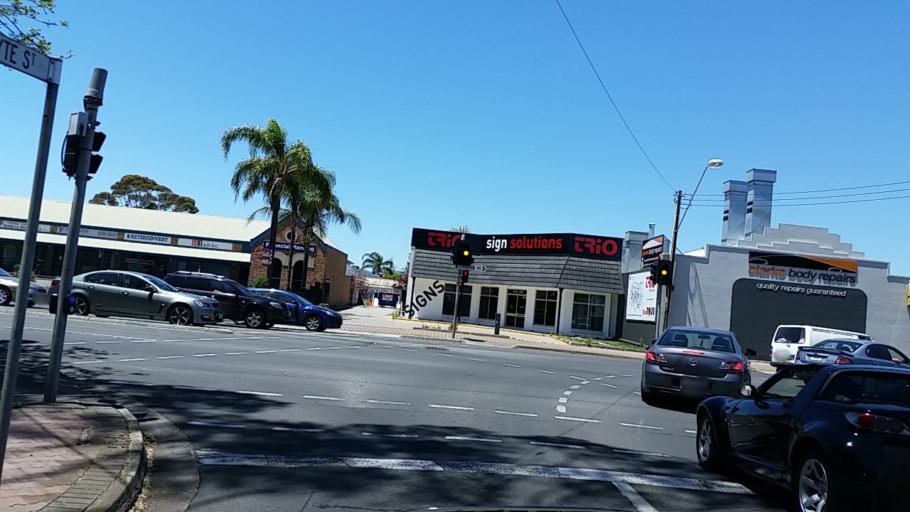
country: AU
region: South Australia
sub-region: Holdfast Bay
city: North Brighton
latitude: -34.9967
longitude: 138.5212
